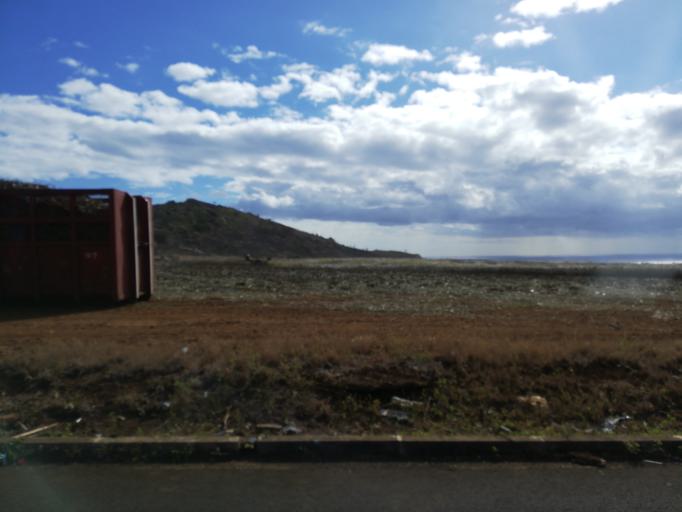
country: MU
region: Black River
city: Gros Cailloux
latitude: -20.2267
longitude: 57.4544
